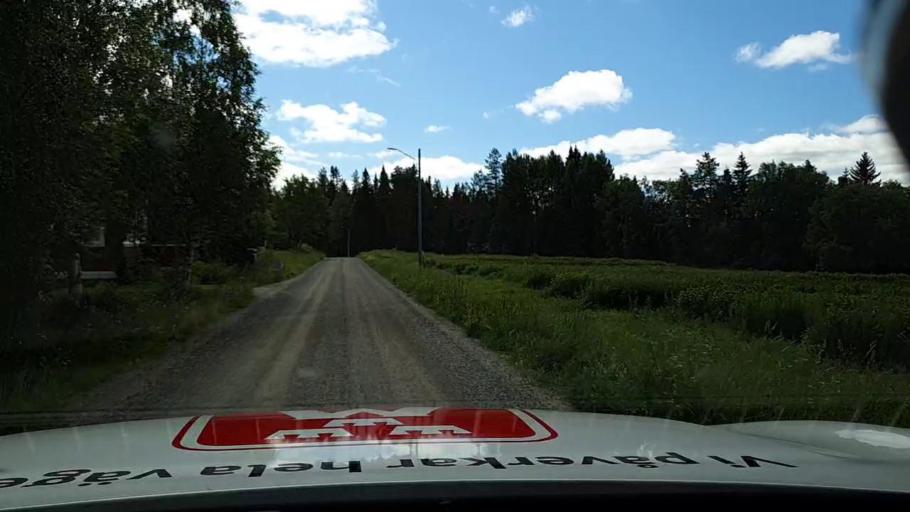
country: SE
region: Jaemtland
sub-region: Braecke Kommun
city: Braecke
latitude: 62.7596
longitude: 15.4998
